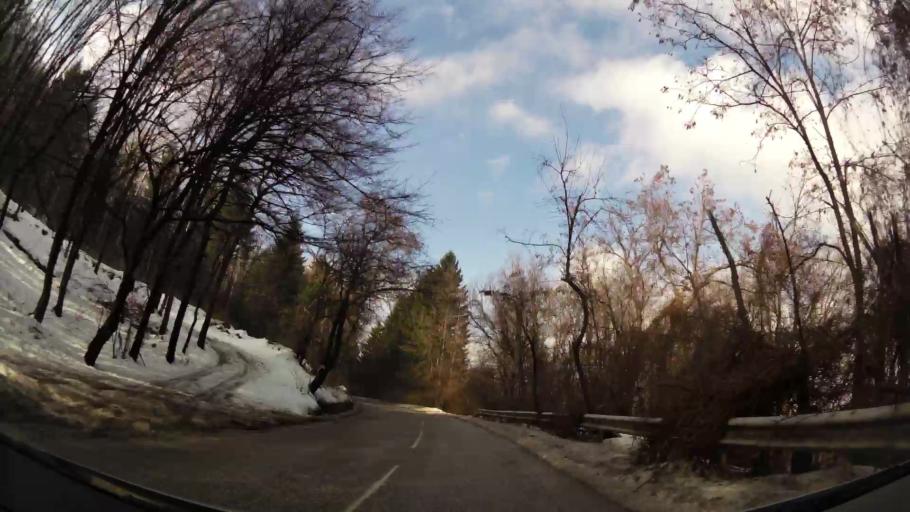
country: BG
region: Sofia-Capital
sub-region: Stolichna Obshtina
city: Sofia
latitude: 42.6460
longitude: 23.2482
